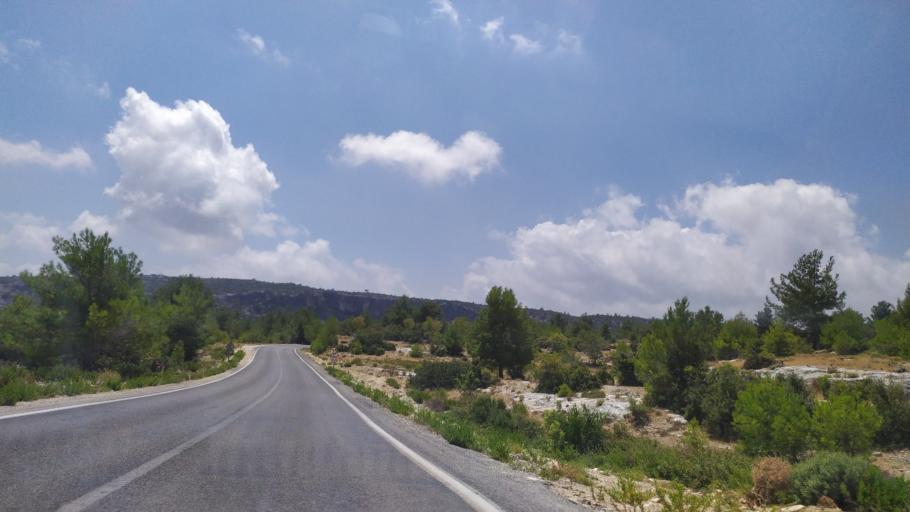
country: TR
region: Mersin
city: Gulnar
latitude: 36.2793
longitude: 33.3889
